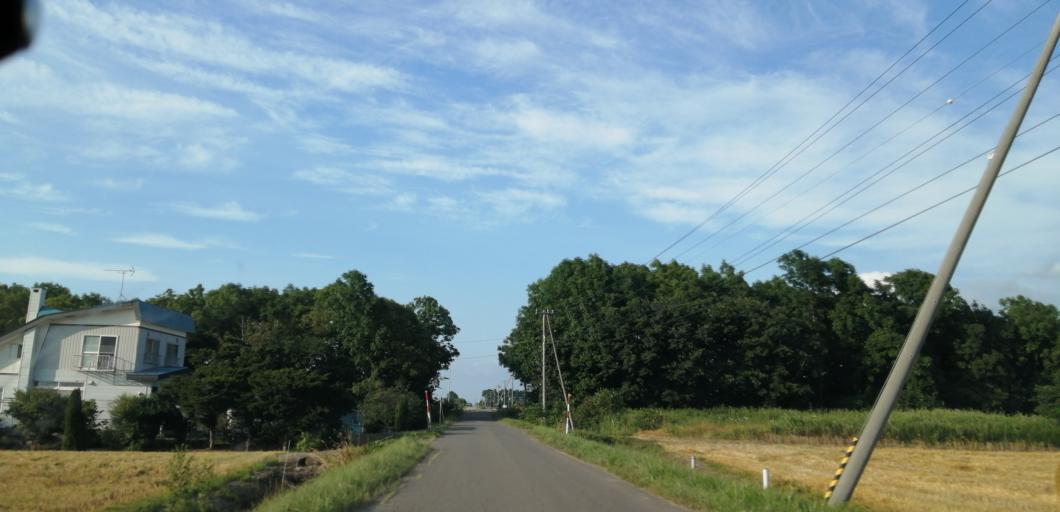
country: JP
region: Hokkaido
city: Kitahiroshima
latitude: 42.9725
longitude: 141.6517
